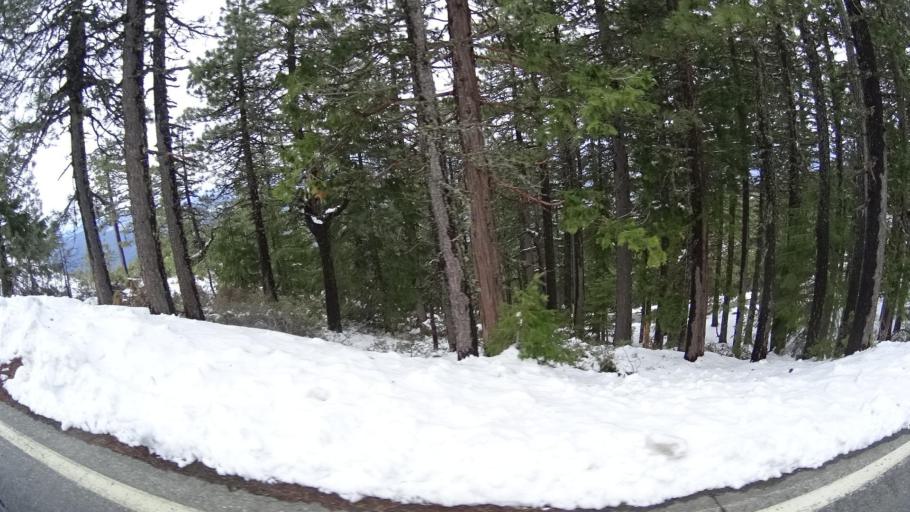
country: US
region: California
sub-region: Humboldt County
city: Willow Creek
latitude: 40.8662
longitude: -123.7365
